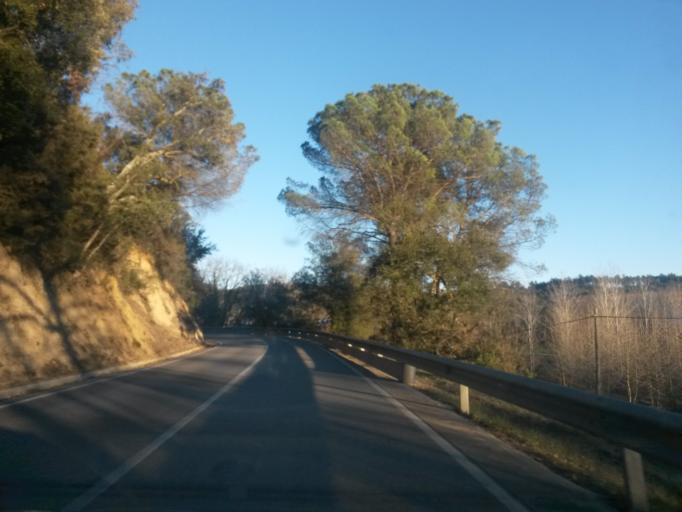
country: ES
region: Catalonia
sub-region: Provincia de Girona
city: Massanes
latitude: 41.7628
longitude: 2.6919
